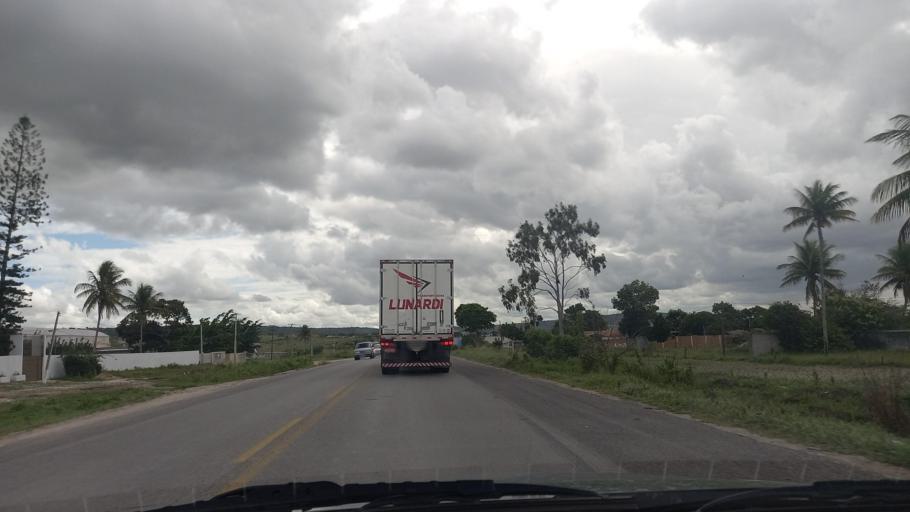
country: BR
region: Pernambuco
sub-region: Lajedo
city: Lajedo
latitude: -8.6636
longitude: -36.3534
